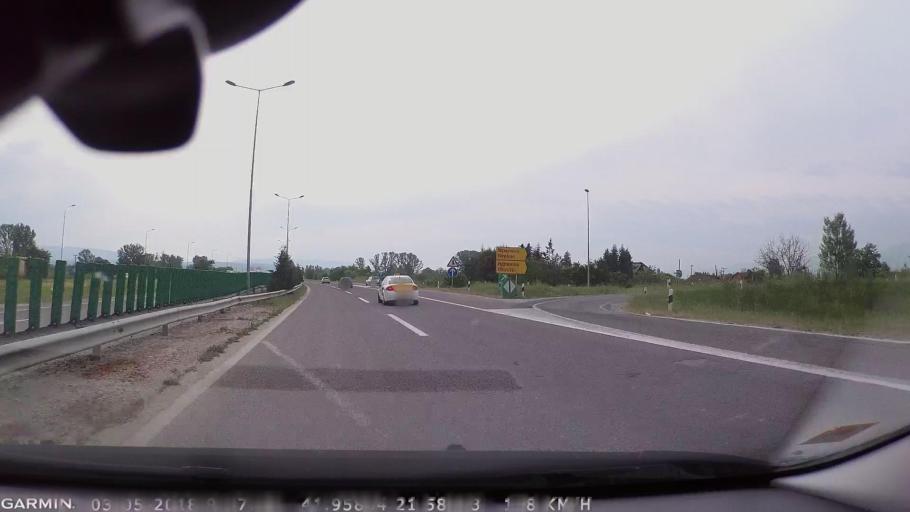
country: MK
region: Ilinden
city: Idrizovo
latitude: 41.9691
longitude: 21.5708
